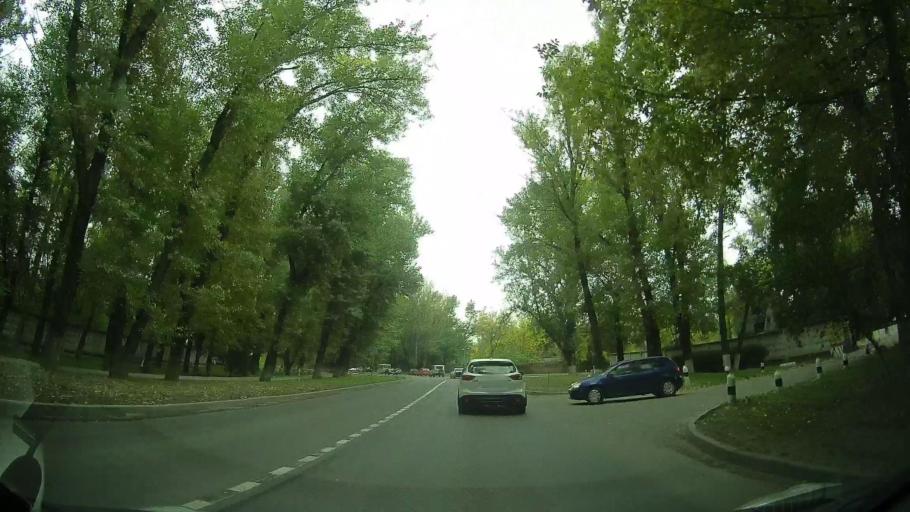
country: RU
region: Rostov
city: Severnyy
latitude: 47.2726
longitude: 39.6647
